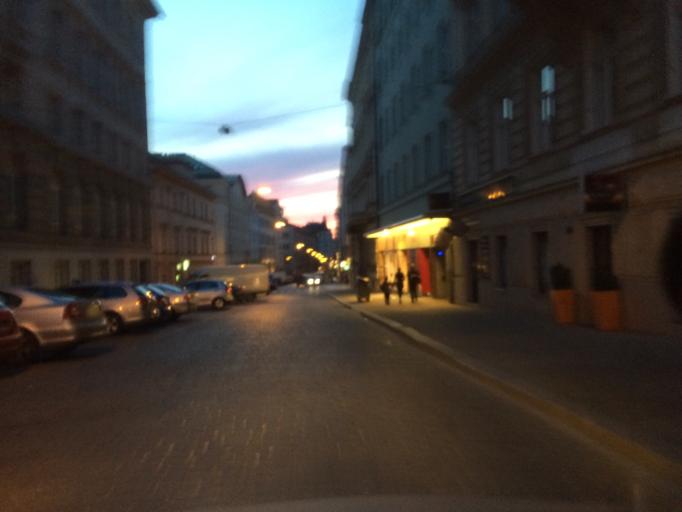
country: CZ
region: Praha
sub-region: Praha 1
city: Stare Mesto
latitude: 50.0814
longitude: 14.4316
